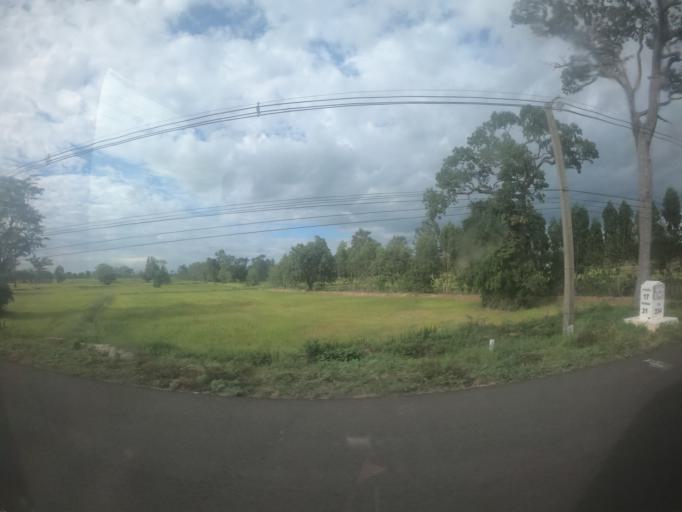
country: TH
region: Surin
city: Prasat
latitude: 14.5808
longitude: 103.4771
